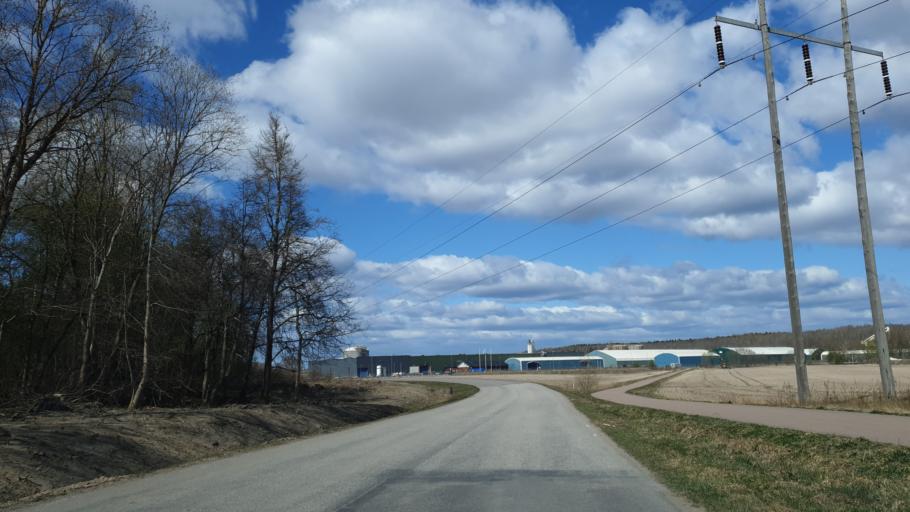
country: SE
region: Vaestmanland
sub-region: Kopings Kommun
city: Koping
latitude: 59.4950
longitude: 16.0221
